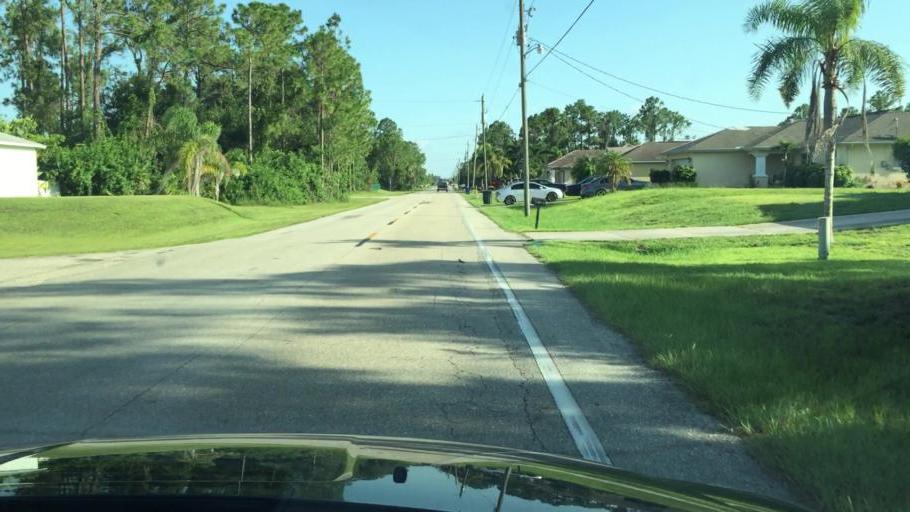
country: US
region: Florida
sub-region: Lee County
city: Buckingham
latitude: 26.6347
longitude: -81.7506
